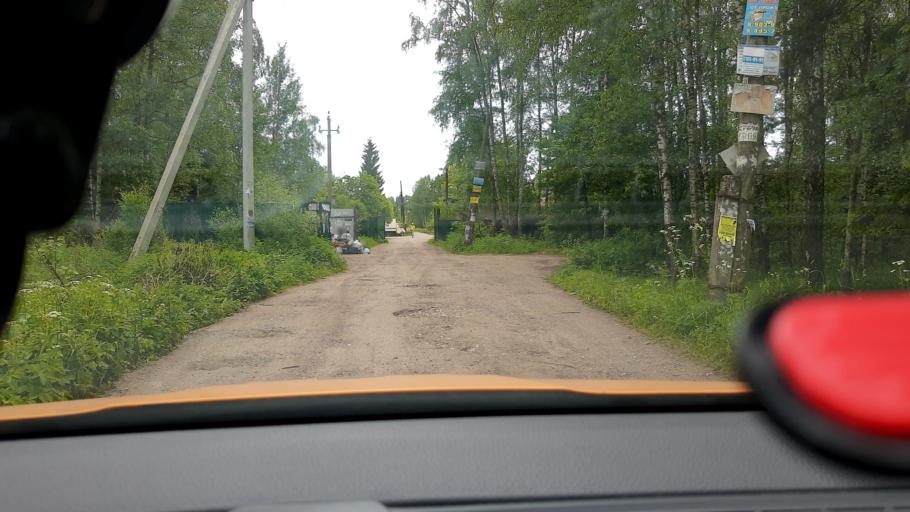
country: RU
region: Moskovskaya
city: Chupryakovo
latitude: 55.5667
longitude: 36.6601
